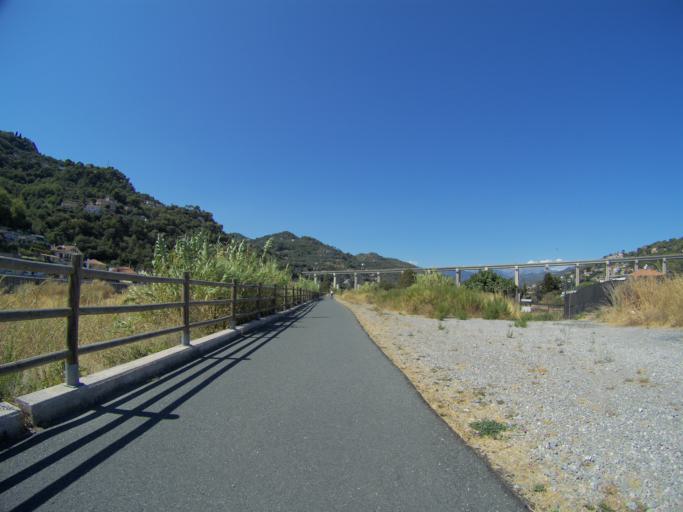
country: IT
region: Liguria
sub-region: Provincia di Imperia
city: Vallecrosia
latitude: 43.7970
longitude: 7.6288
